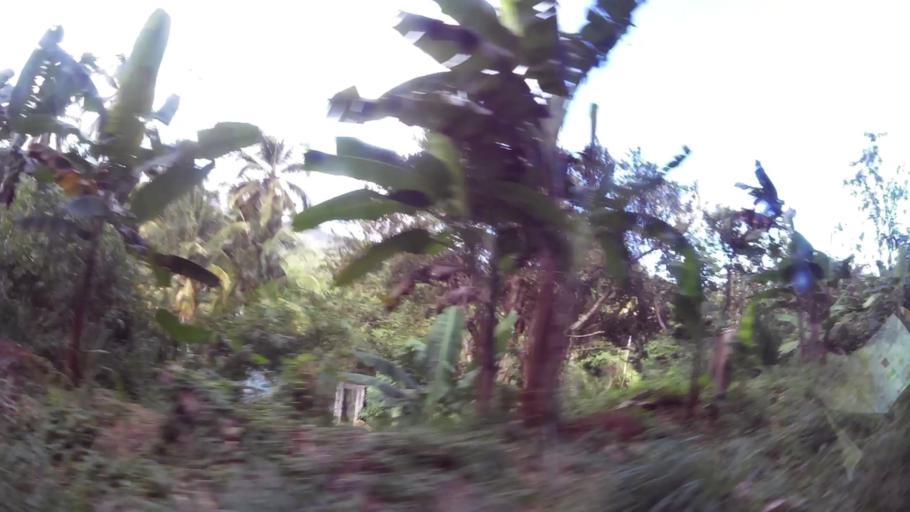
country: DM
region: Saint Andrew
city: Marigot
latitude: 15.5167
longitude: -61.2752
